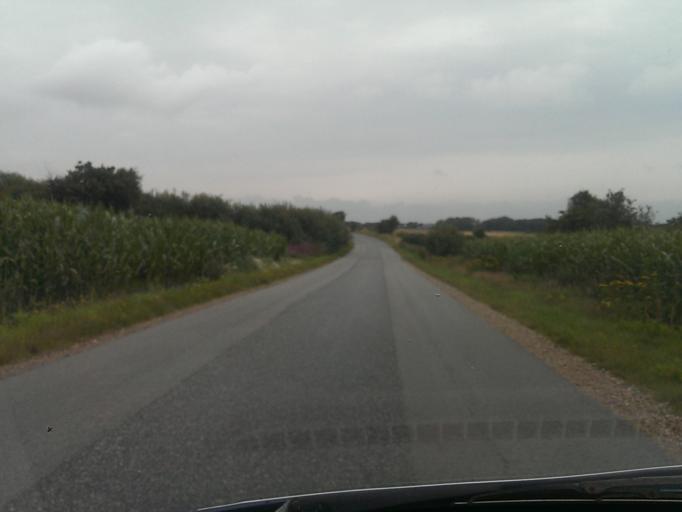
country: DK
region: South Denmark
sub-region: Esbjerg Kommune
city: Tjaereborg
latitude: 55.5079
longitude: 8.5753
